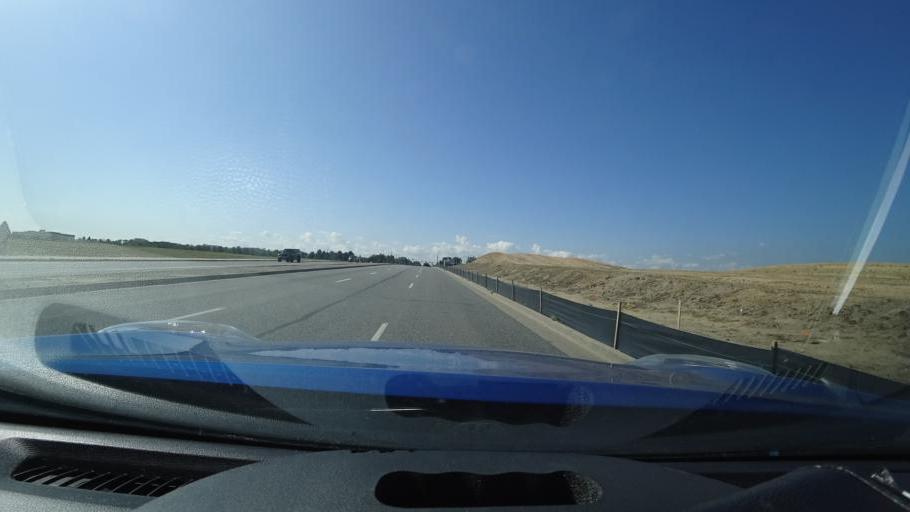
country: US
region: Colorado
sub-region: Adams County
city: Aurora
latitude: 39.7093
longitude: -104.7912
